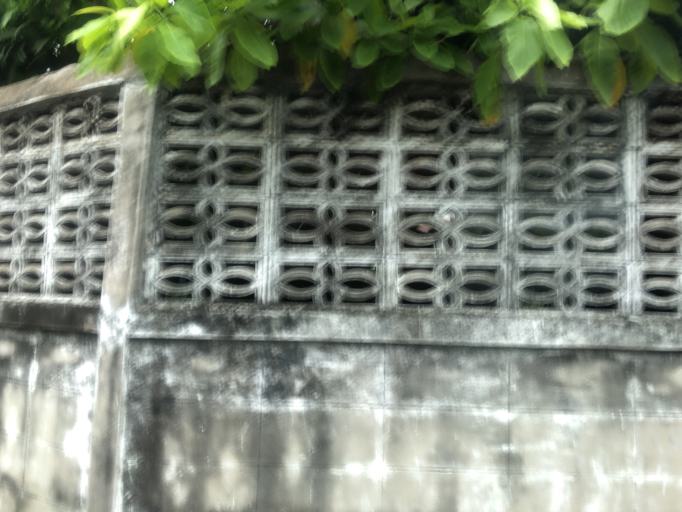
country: TH
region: Bangkok
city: Don Mueang
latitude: 13.9242
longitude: 100.5919
